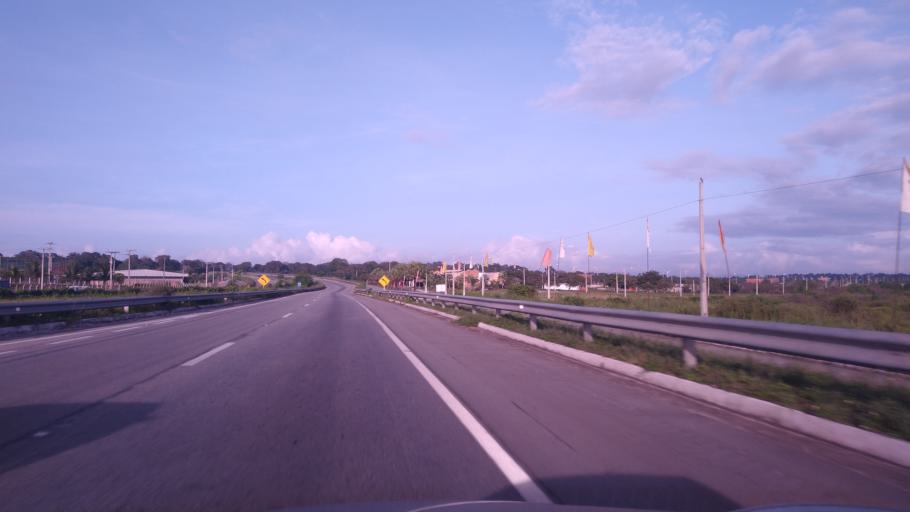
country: BR
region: Ceara
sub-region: Pacajus
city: Pacajus
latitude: -4.1650
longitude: -38.4896
